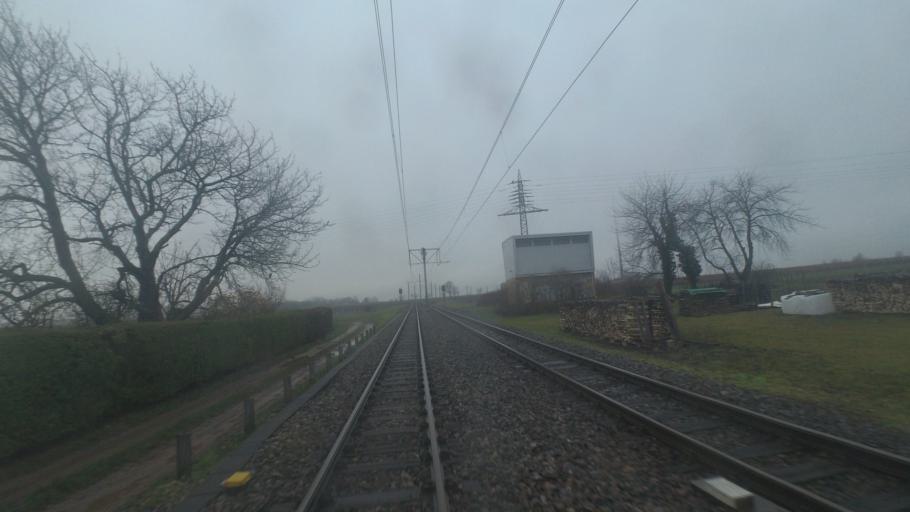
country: DE
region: Rheinland-Pfalz
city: Gonnheim
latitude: 49.4578
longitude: 8.2311
